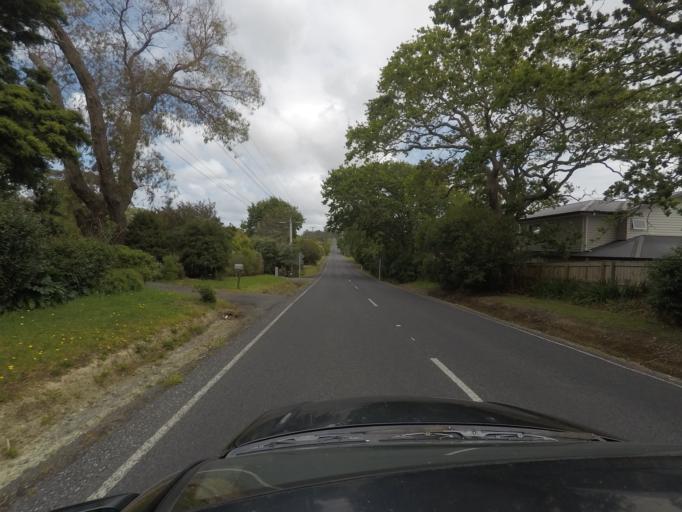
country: NZ
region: Auckland
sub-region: Auckland
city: Parakai
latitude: -36.6279
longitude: 174.5022
